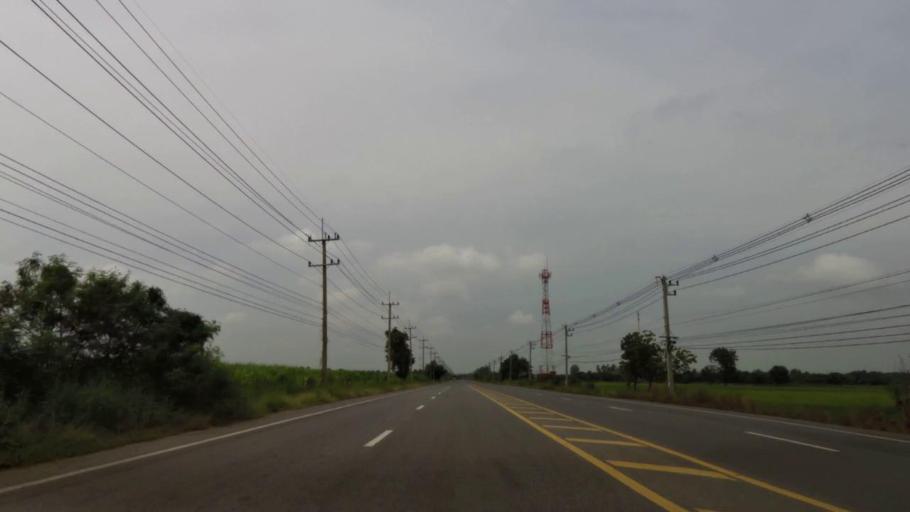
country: TH
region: Lop Buri
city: Khok Samrong
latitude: 15.0646
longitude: 100.6399
